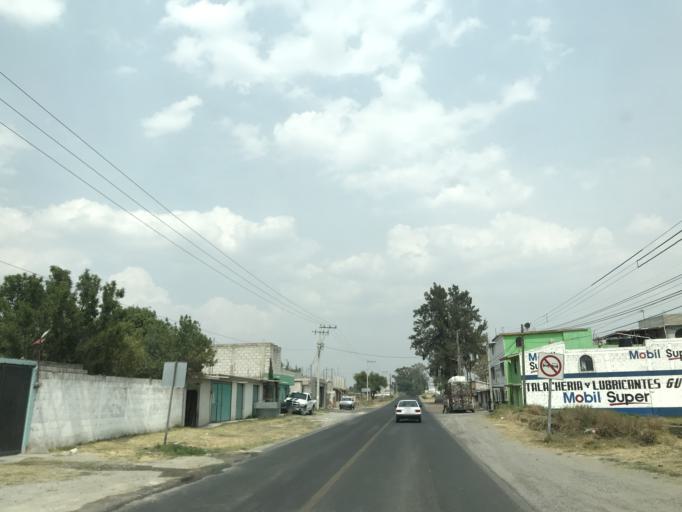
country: MX
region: Tlaxcala
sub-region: Panotla
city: Fraccionamiento la Virgen
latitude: 19.3201
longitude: -98.2828
